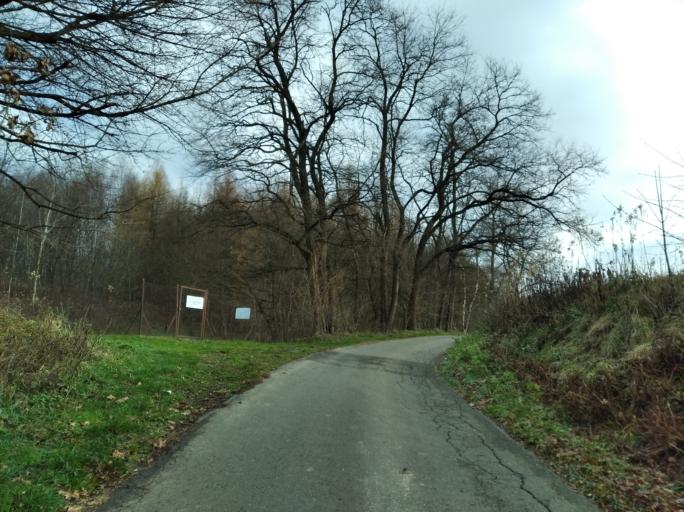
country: PL
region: Subcarpathian Voivodeship
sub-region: Powiat strzyzowski
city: Strzyzow
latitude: 49.8781
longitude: 21.8250
